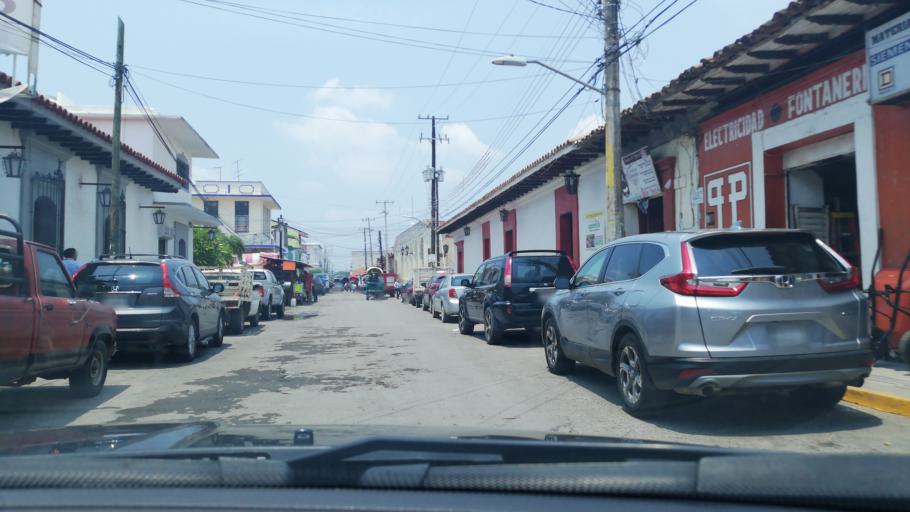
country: MX
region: Oaxaca
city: San Blas Atempa
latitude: 16.3341
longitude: -95.2321
